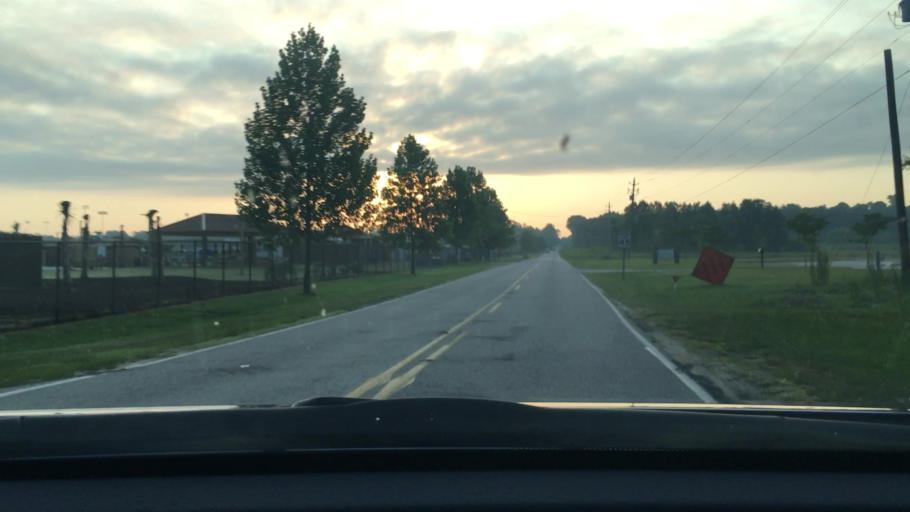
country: US
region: South Carolina
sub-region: Darlington County
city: Hartsville
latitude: 34.3499
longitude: -80.0929
